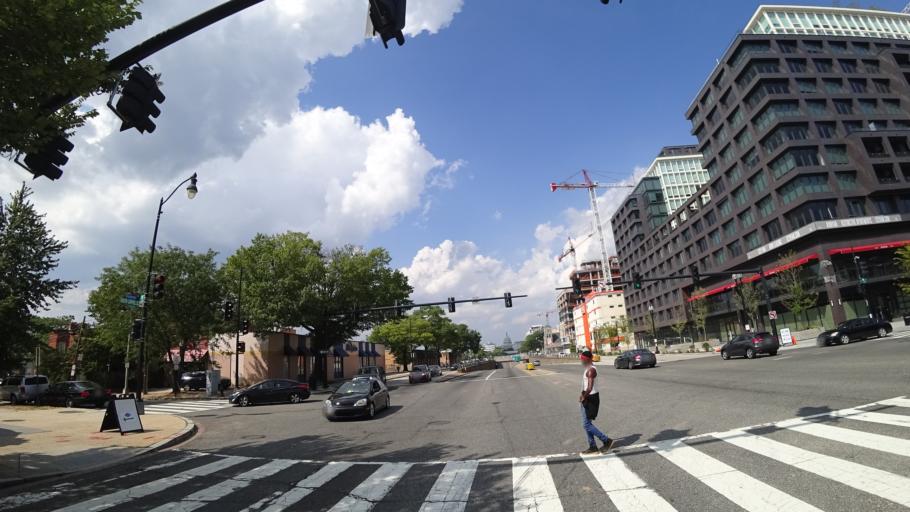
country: US
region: Washington, D.C.
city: Washington, D.C.
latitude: 38.8745
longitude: -77.0091
